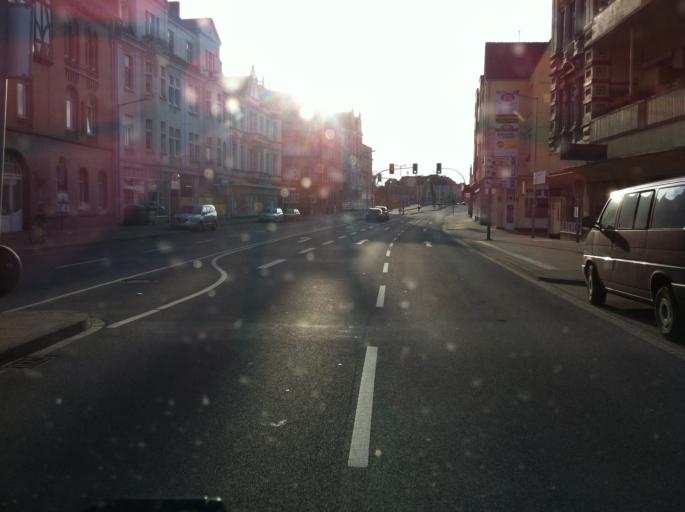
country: DE
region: North Rhine-Westphalia
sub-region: Regierungsbezirk Detmold
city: Minden
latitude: 52.2895
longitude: 8.9280
